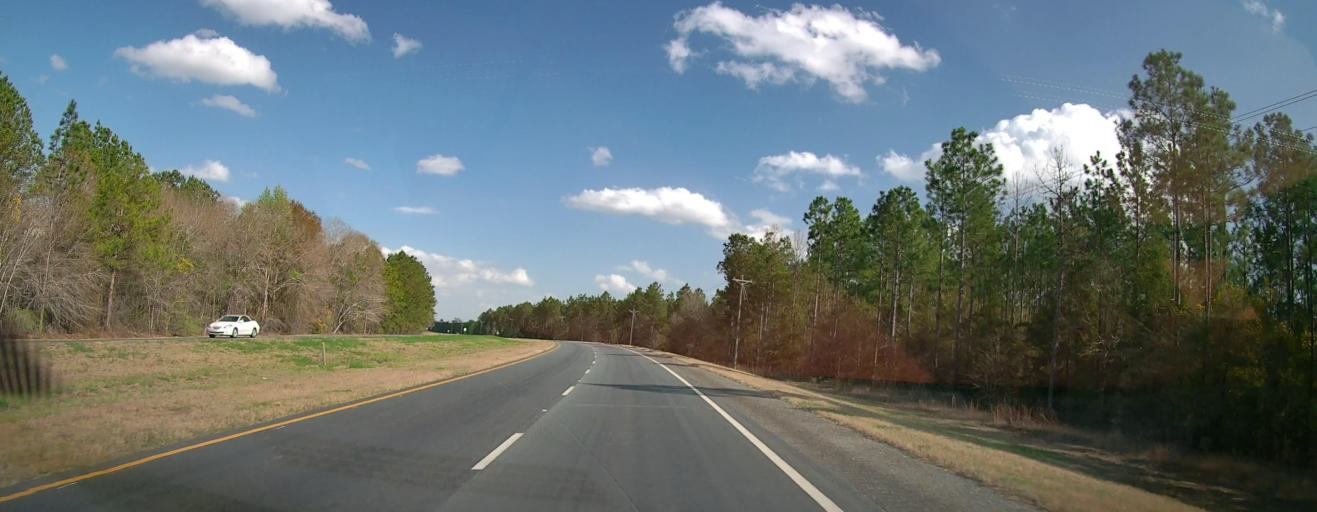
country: US
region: Georgia
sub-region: Dodge County
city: Eastman
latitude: 32.1095
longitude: -83.0928
